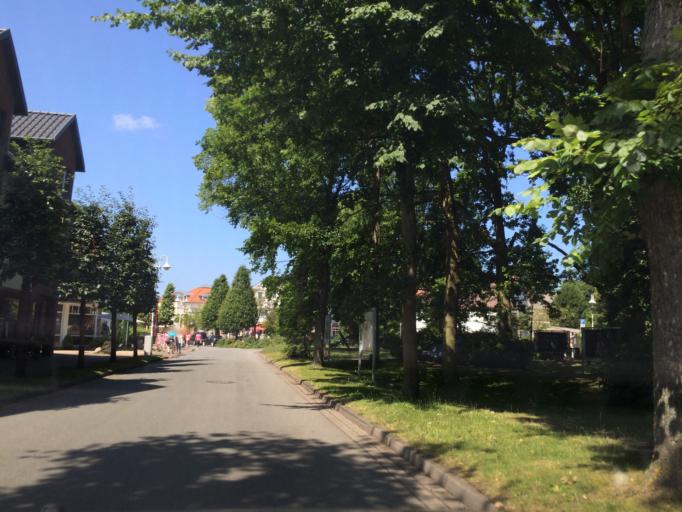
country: DE
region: Mecklenburg-Vorpommern
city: Zingst
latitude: 54.4351
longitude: 12.6866
